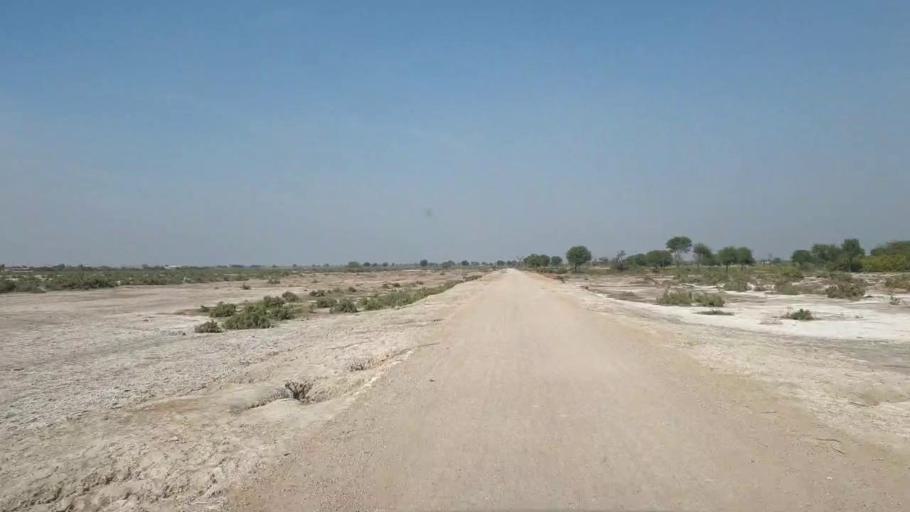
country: PK
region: Sindh
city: Chambar
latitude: 25.3272
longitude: 68.8098
